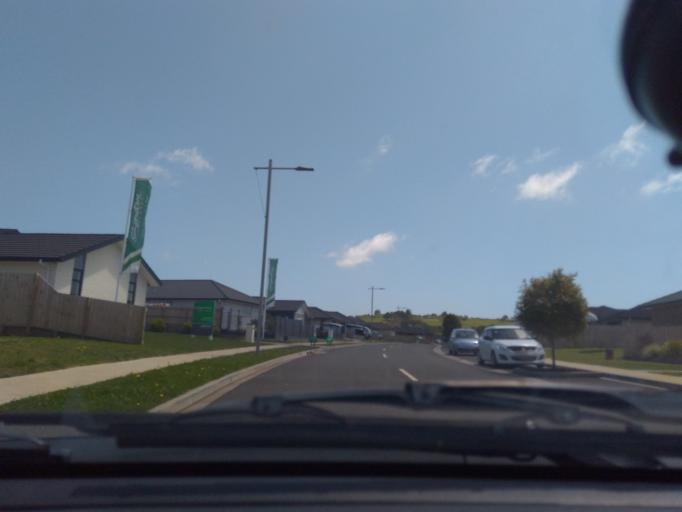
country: NZ
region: Northland
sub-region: Whangarei
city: Whangarei
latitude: -35.6757
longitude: 174.3196
